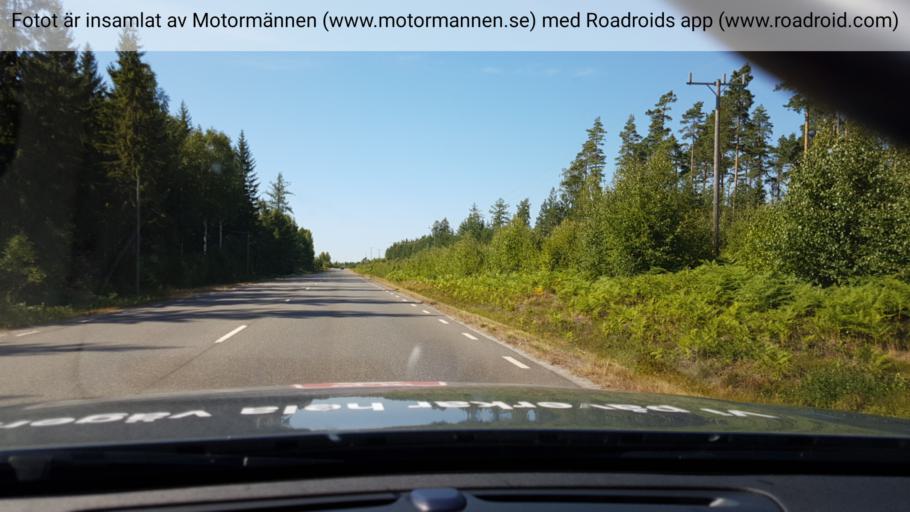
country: SE
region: Vaestra Goetaland
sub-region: Karlsborgs Kommun
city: Molltorp
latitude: 58.5904
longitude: 14.4120
